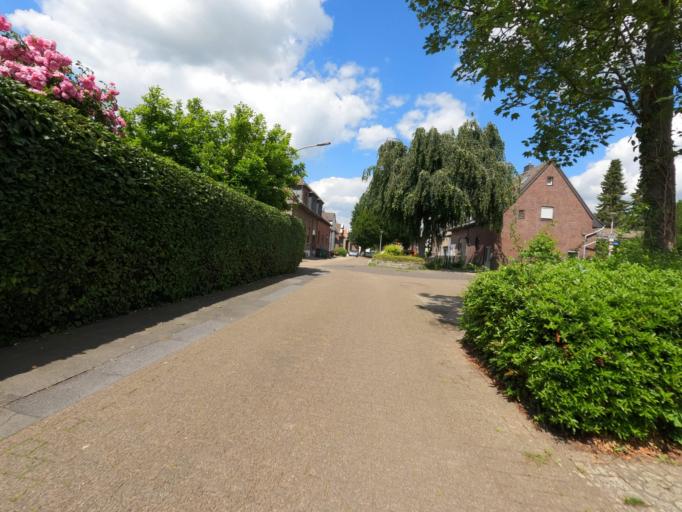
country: DE
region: North Rhine-Westphalia
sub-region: Regierungsbezirk Koln
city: Ubach-Palenberg
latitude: 50.9398
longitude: 6.1087
